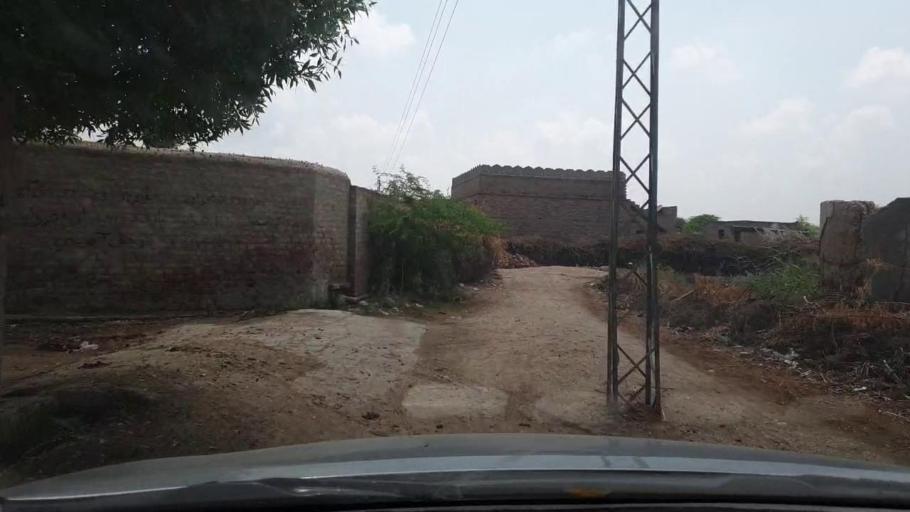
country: PK
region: Sindh
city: Khairpur
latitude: 27.4774
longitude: 68.6921
